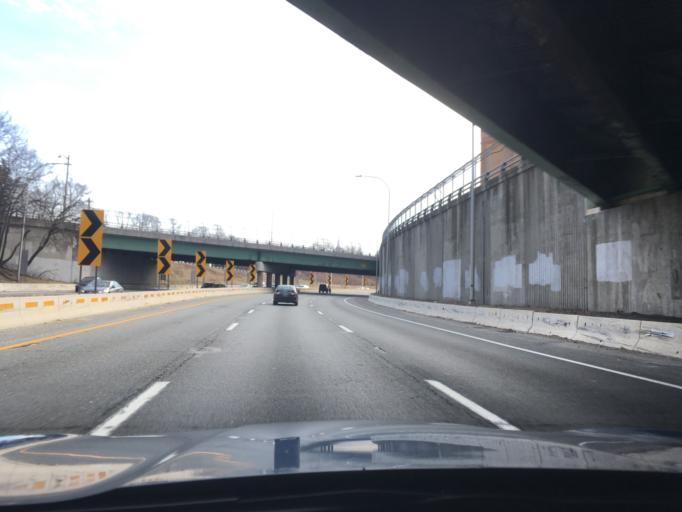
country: US
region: Rhode Island
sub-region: Providence County
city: Pawtucket
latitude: 41.8833
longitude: -71.3781
